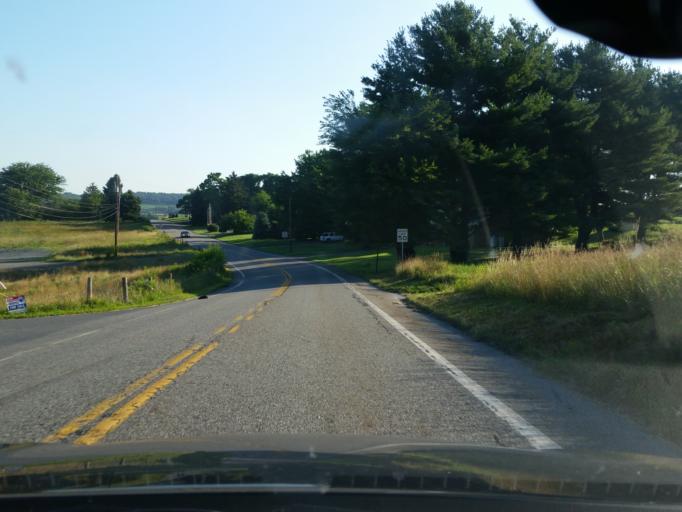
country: US
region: Pennsylvania
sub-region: Dauphin County
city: Matamoras
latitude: 40.4185
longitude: -76.9427
